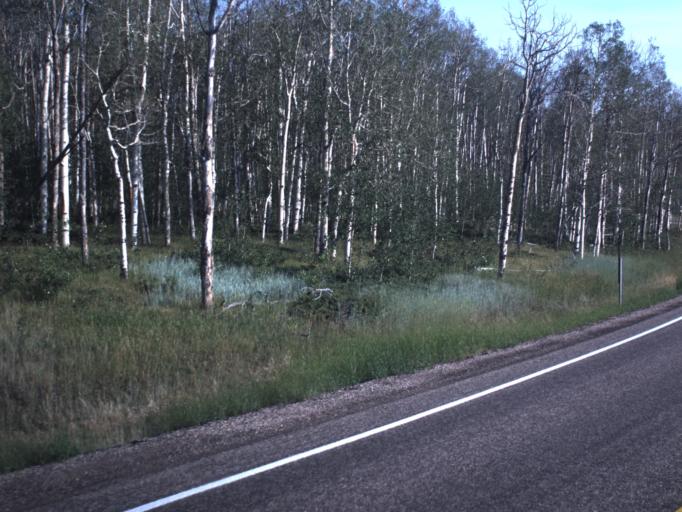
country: US
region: Utah
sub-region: Uintah County
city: Maeser
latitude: 40.7178
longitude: -109.4734
